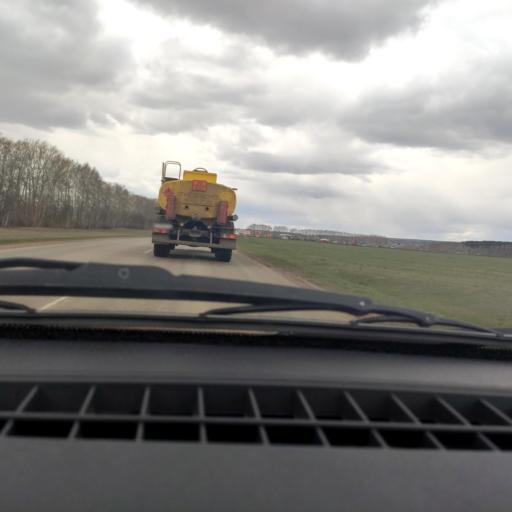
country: RU
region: Bashkortostan
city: Chekmagush
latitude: 55.1275
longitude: 54.6966
